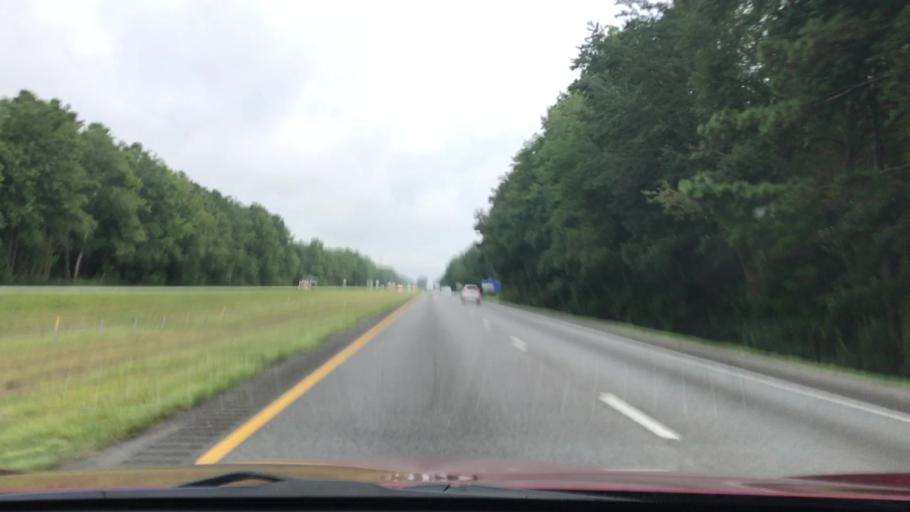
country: US
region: South Carolina
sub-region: Dorchester County
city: Ridgeville
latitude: 33.1317
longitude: -80.2987
